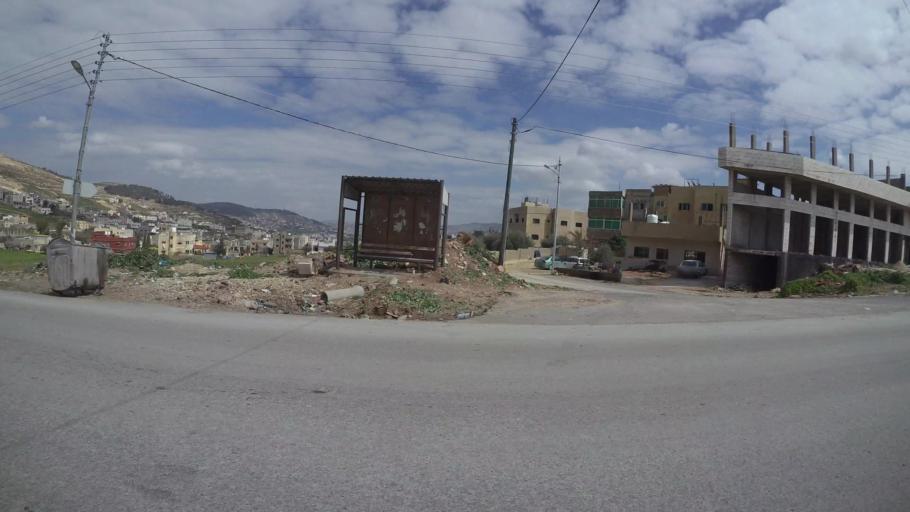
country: JO
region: Amman
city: Al Jubayhah
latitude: 32.0617
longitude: 35.8088
